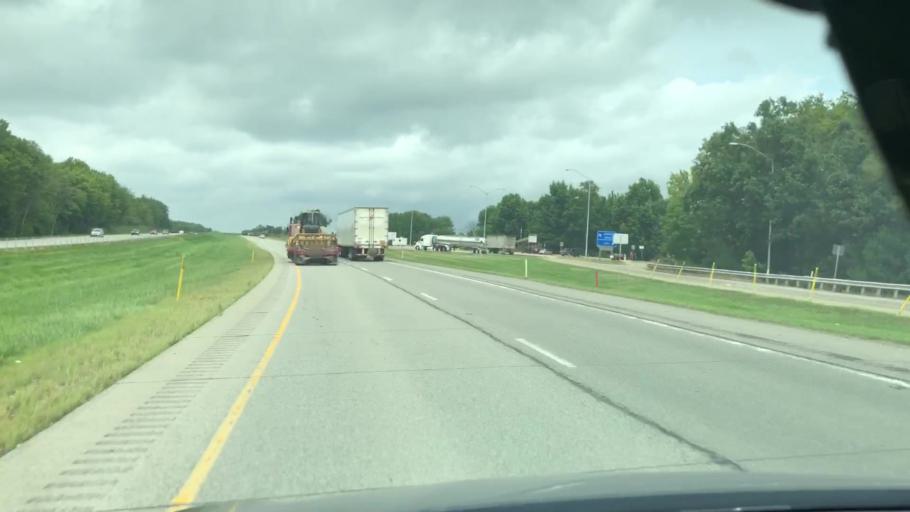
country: US
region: Pennsylvania
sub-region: Butler County
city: Slippery Rock
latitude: 41.0685
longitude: -80.1237
